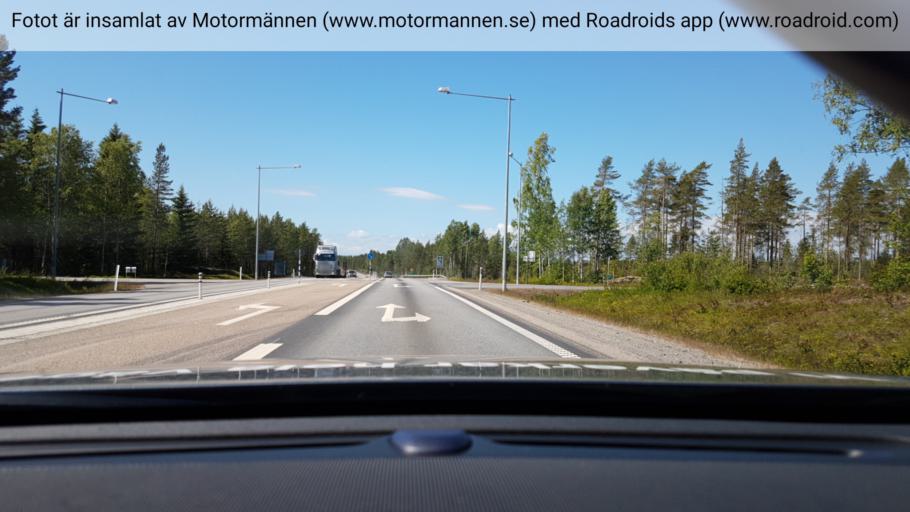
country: SE
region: Vaesterbotten
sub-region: Umea Kommun
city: Hoernefors
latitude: 63.6139
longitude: 19.8061
